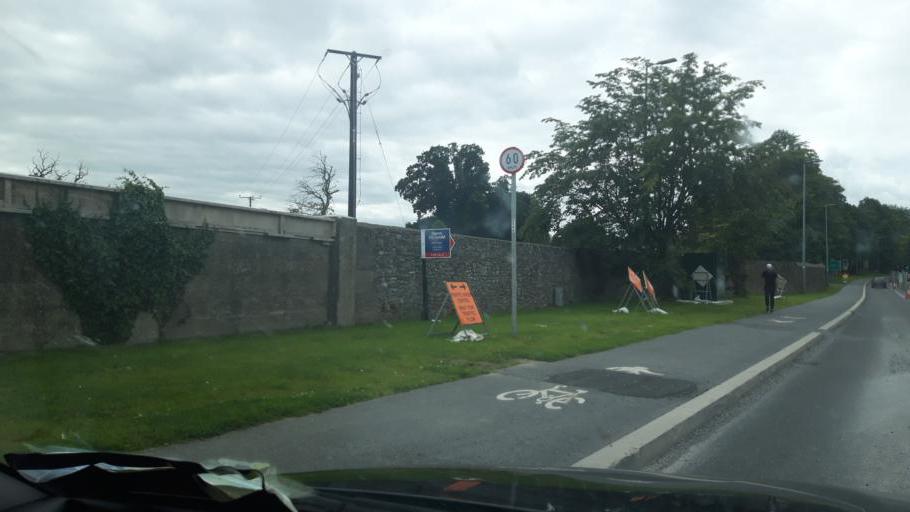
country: IE
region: Leinster
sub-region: Kilkenny
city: Kilkenny
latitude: 52.6406
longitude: -7.2672
